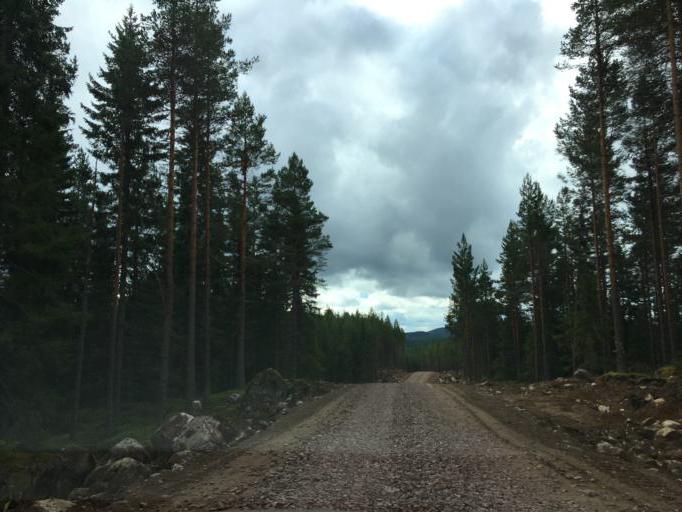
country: SE
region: OErebro
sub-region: Hallefors Kommun
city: Haellefors
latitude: 60.0789
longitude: 14.4732
